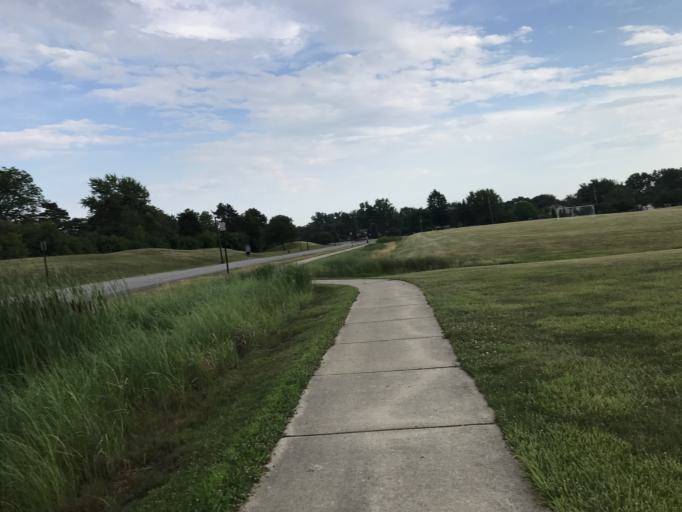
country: US
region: Michigan
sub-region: Oakland County
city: Franklin
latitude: 42.4875
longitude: -83.3293
